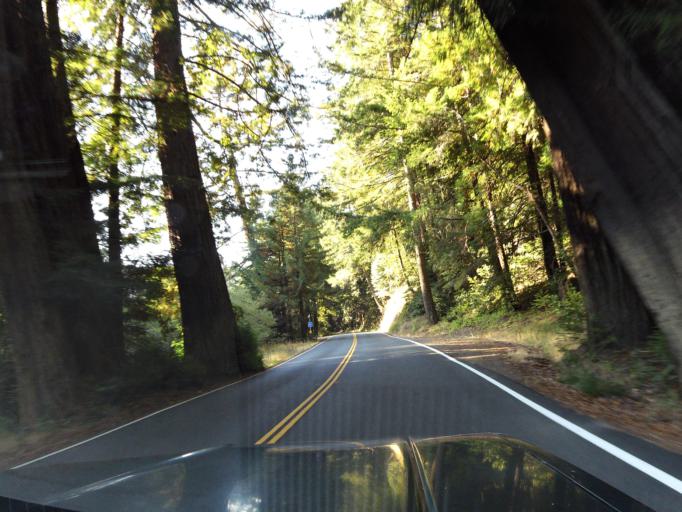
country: US
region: California
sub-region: Mendocino County
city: Boonville
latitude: 39.1616
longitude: -123.6385
